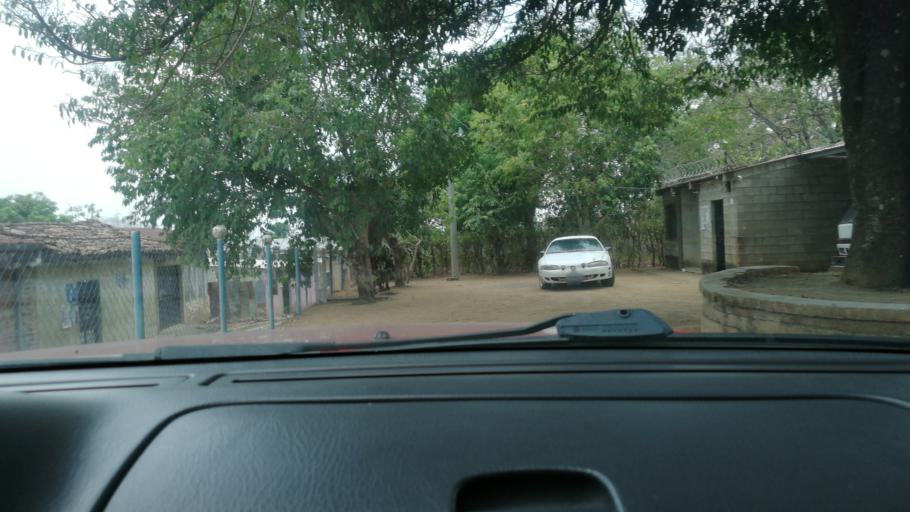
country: SV
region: Ahuachapan
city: Tacuba
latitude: 13.9047
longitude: -89.9078
